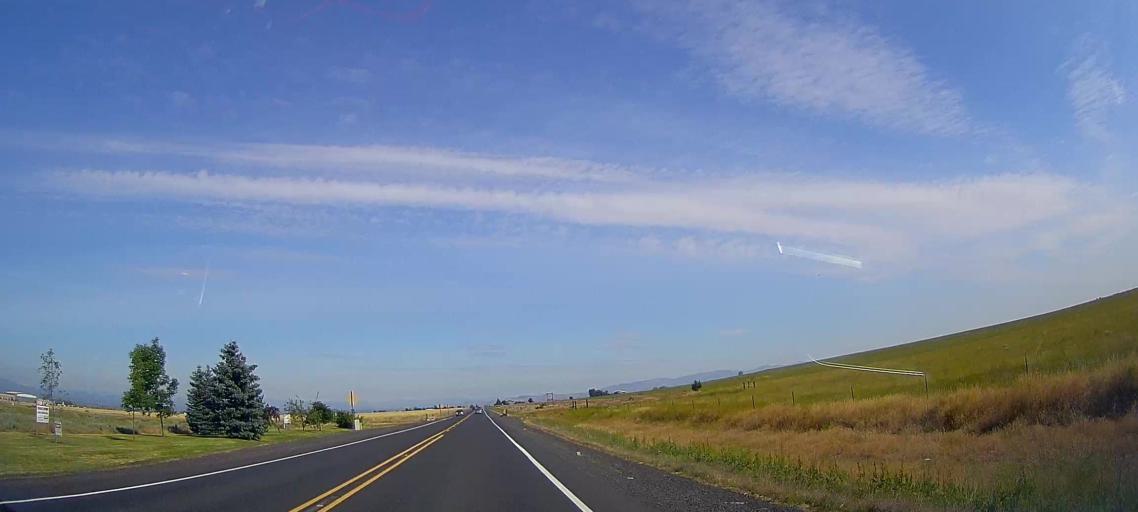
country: US
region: Oregon
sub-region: Jefferson County
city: Madras
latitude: 44.6682
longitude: -121.1383
